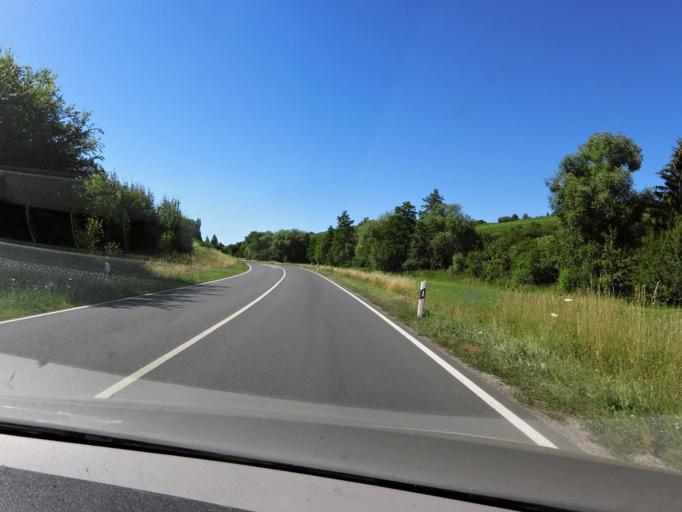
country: DE
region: Bavaria
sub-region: Regierungsbezirk Unterfranken
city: Buchbrunn
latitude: 49.7436
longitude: 10.1342
